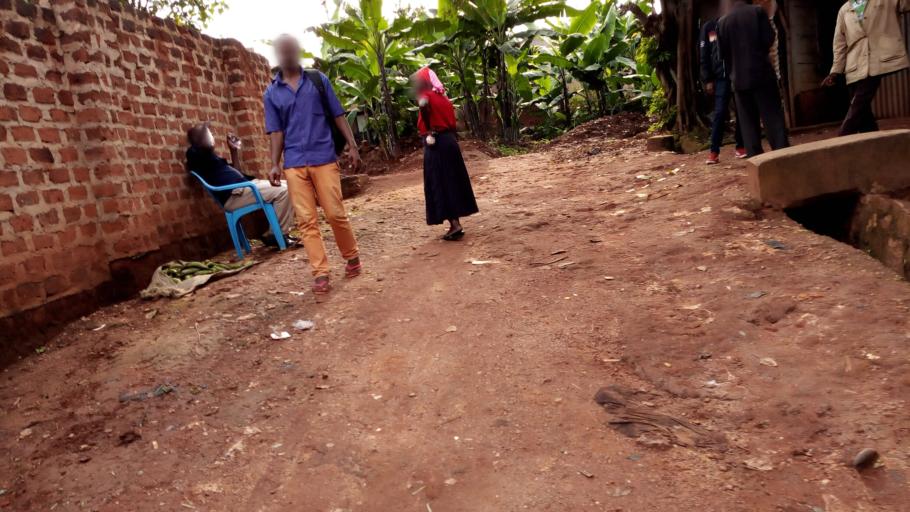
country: UG
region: Central Region
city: Kampala Central Division
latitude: 0.3717
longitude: 32.5545
